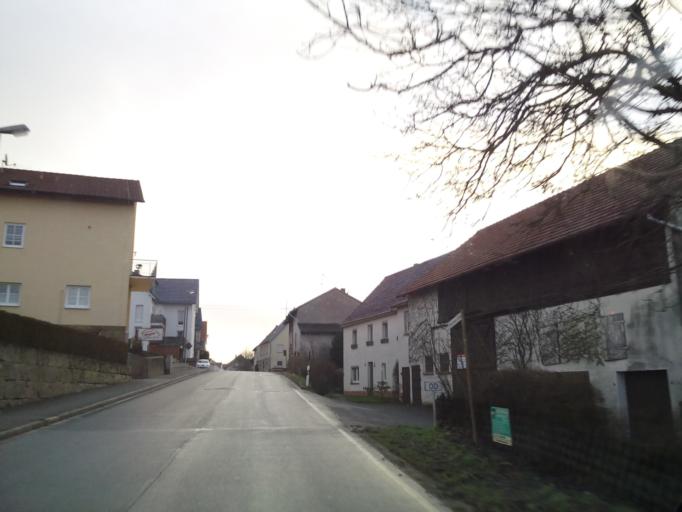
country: DE
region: Bavaria
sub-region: Upper Franconia
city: Untersiemau
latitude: 50.1855
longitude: 11.0084
